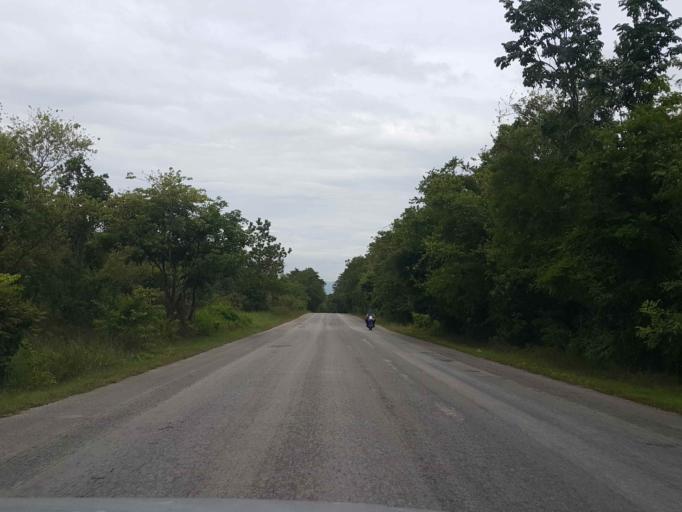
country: TH
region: Lampang
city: Thoen
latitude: 17.6301
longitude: 99.2639
